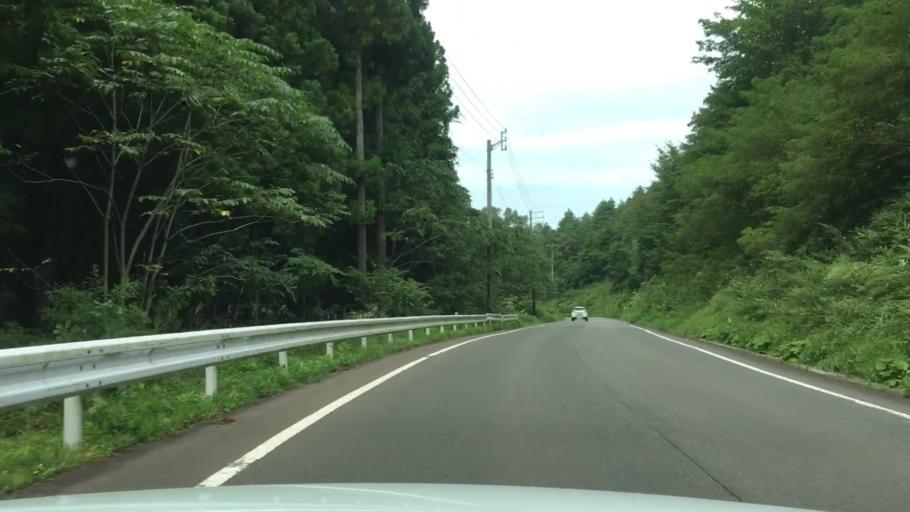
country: JP
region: Aomori
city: Shimokizukuri
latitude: 40.7233
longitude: 140.2570
